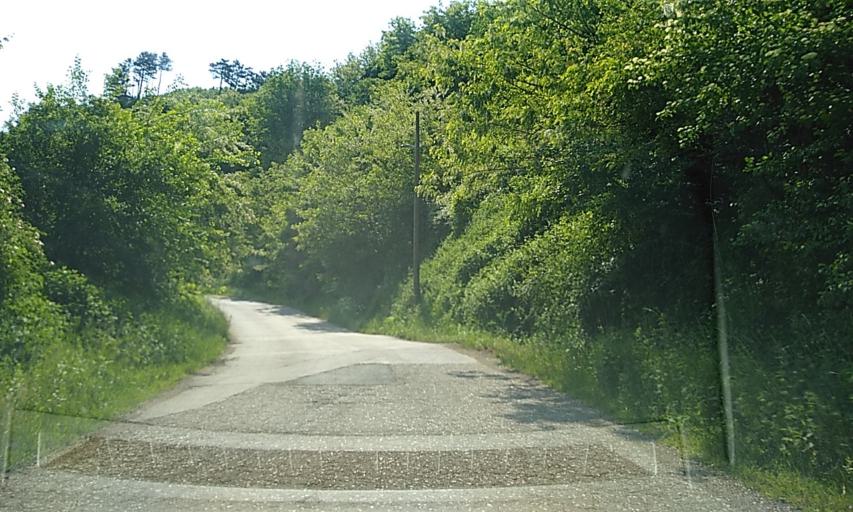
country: RS
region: Central Serbia
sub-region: Pcinjski Okrug
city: Vladicin Han
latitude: 42.7203
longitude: 22.0607
